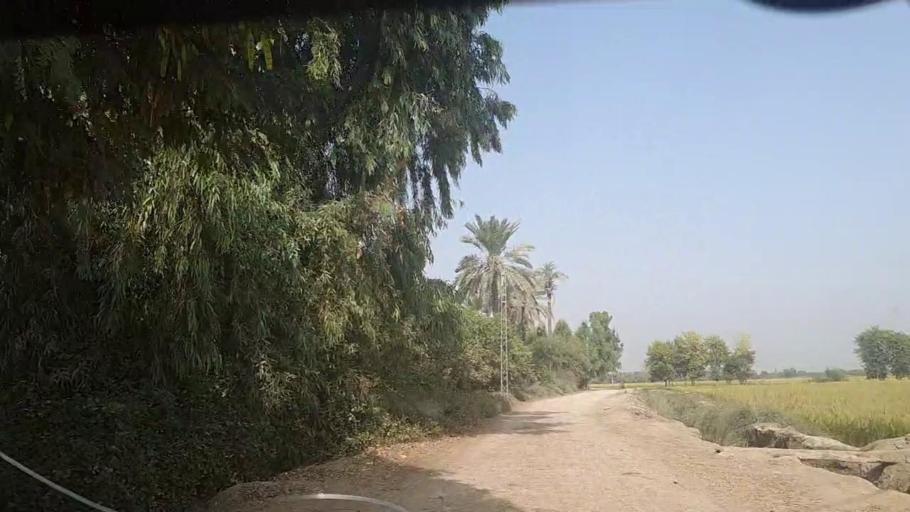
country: PK
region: Sindh
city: Madeji
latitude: 27.8014
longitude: 68.4251
